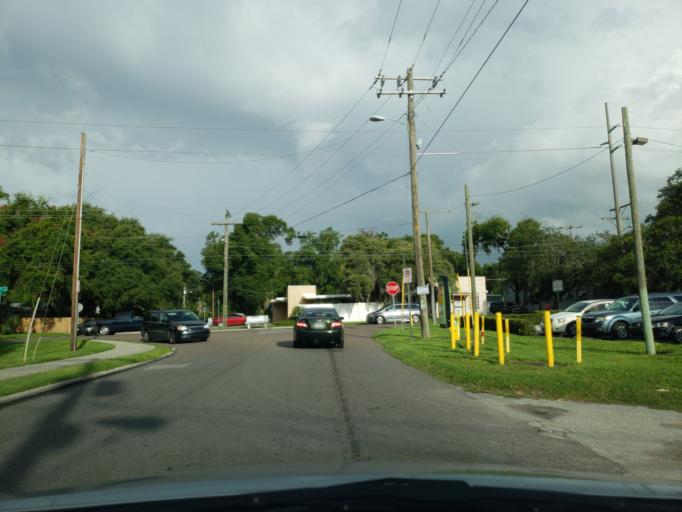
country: US
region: Florida
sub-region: Hillsborough County
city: Temple Terrace
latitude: 27.9998
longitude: -82.4343
